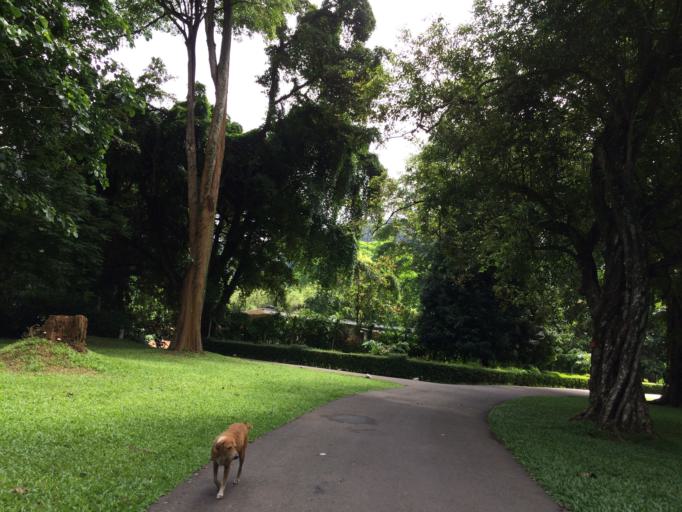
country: LK
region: Central
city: Kandy
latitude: 7.2757
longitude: 80.5928
